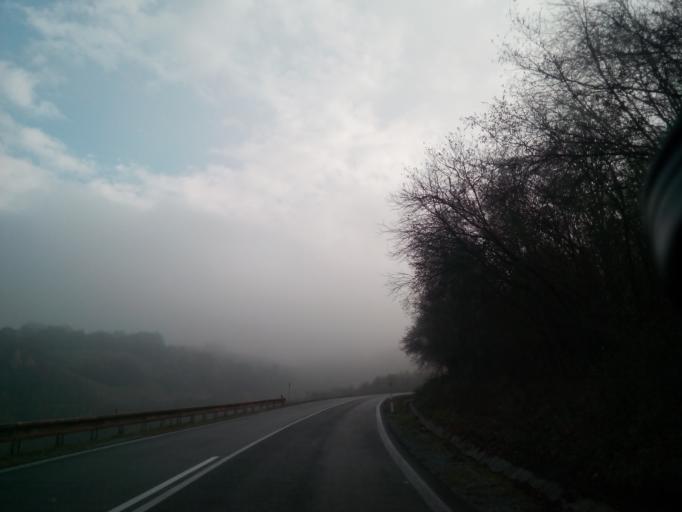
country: SK
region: Kosicky
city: Gelnica
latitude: 48.8528
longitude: 21.0213
